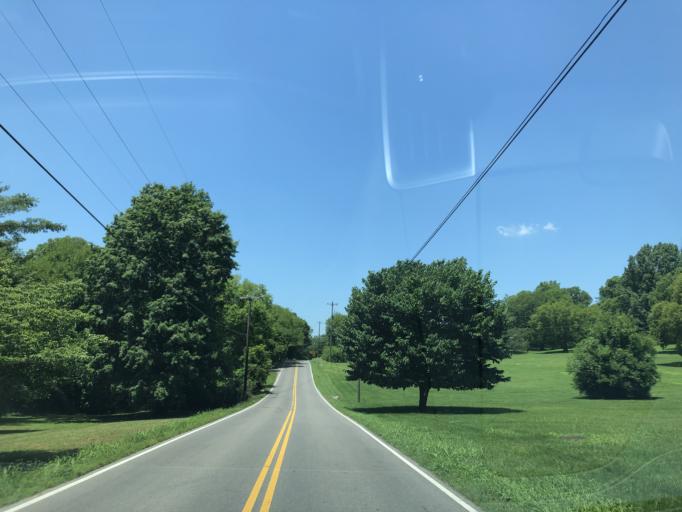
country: US
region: Tennessee
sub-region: Williamson County
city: Nolensville
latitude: 36.0115
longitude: -86.6679
